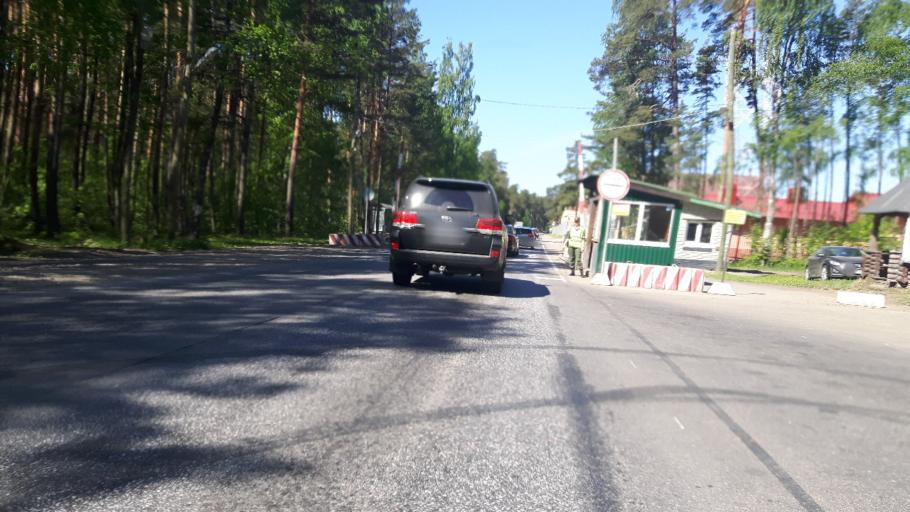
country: RU
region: Leningrad
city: Lebyazh'ye
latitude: 59.9577
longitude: 29.4502
